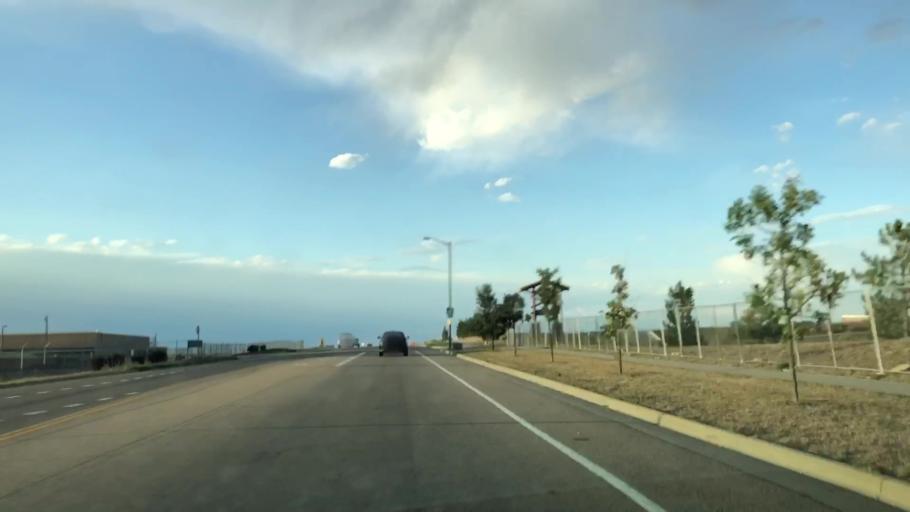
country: US
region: Colorado
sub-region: Larimer County
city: Loveland
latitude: 40.4371
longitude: -104.9958
